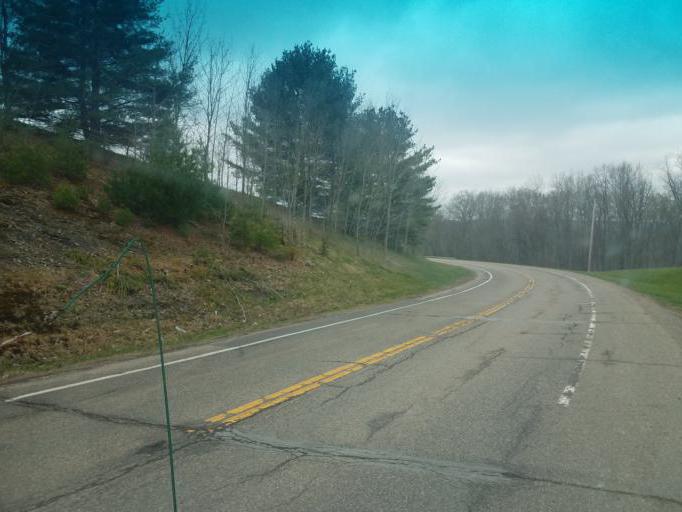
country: US
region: Ohio
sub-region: Stark County
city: Beach City
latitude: 40.6054
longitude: -81.5986
